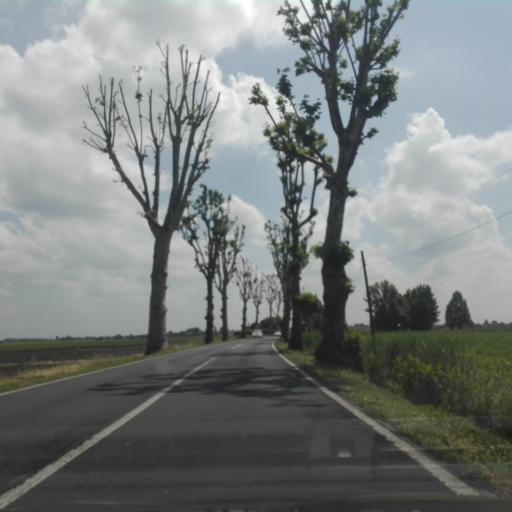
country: IT
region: Veneto
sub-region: Provincia di Rovigo
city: Buso
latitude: 45.0760
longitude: 11.8646
